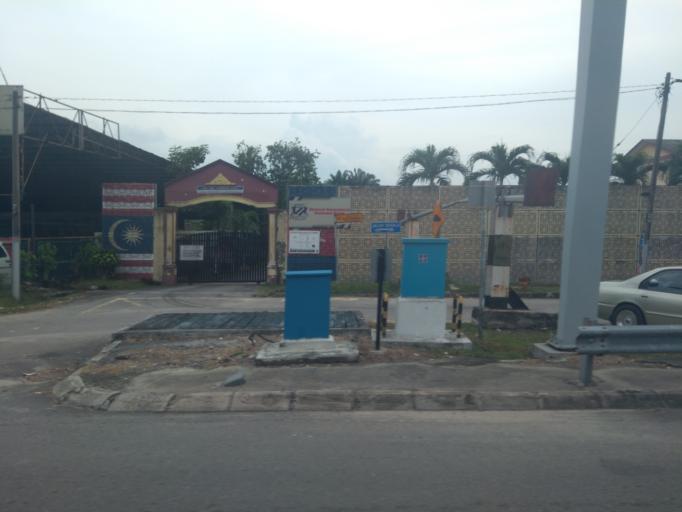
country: MY
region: Johor
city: Skudai
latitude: 1.4987
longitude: 103.6985
